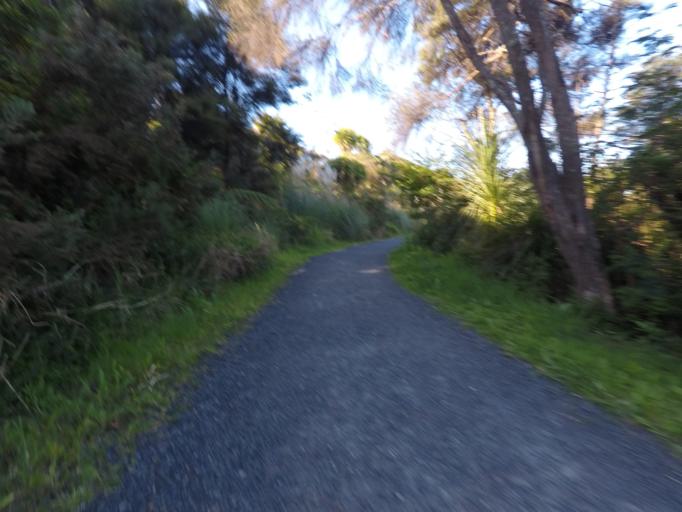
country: NZ
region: Auckland
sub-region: Auckland
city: Rosebank
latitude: -36.8457
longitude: 174.6554
